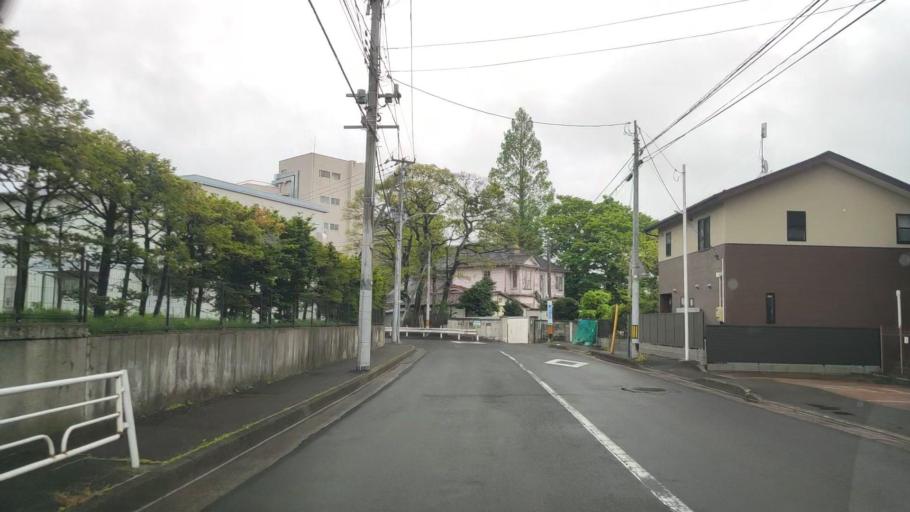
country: JP
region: Miyagi
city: Sendai
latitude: 38.2504
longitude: 140.8751
